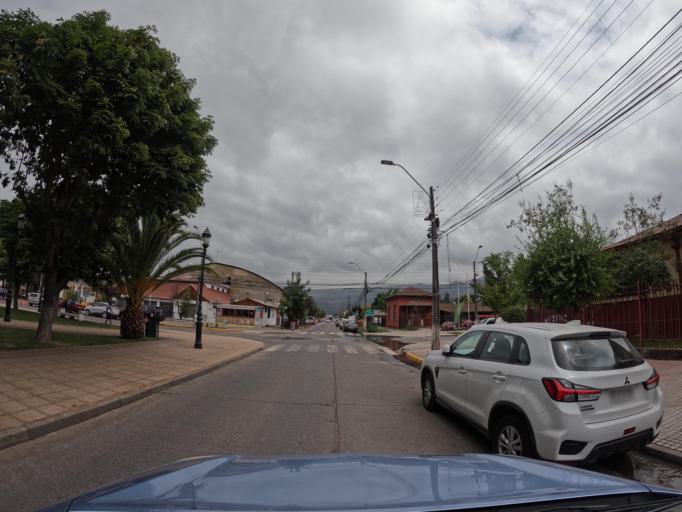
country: CL
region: O'Higgins
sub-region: Provincia de Colchagua
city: Chimbarongo
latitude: -34.7084
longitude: -71.0403
